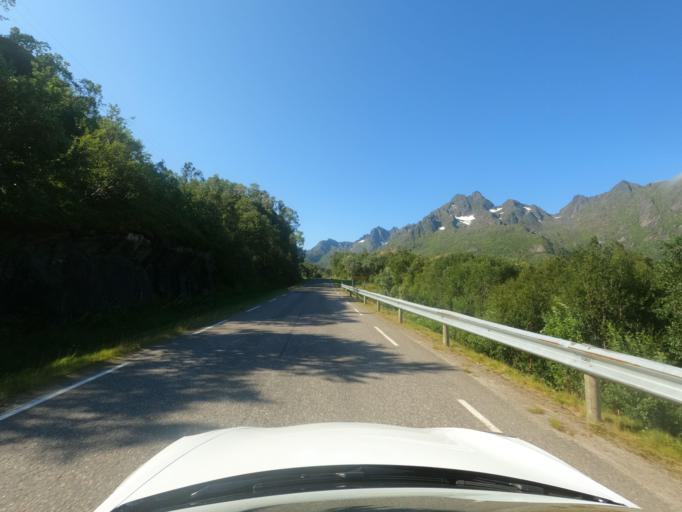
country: NO
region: Nordland
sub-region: Hadsel
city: Stokmarknes
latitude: 68.4349
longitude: 15.1792
